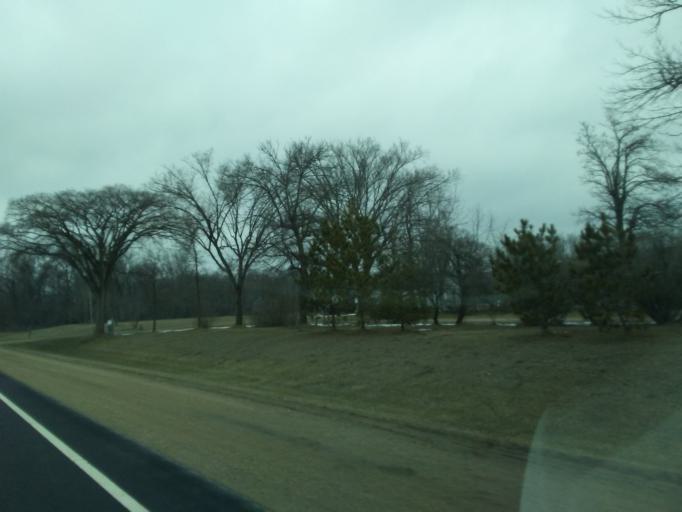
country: US
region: Wisconsin
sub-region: Sauk County
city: Spring Green
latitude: 43.1999
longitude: -90.2421
